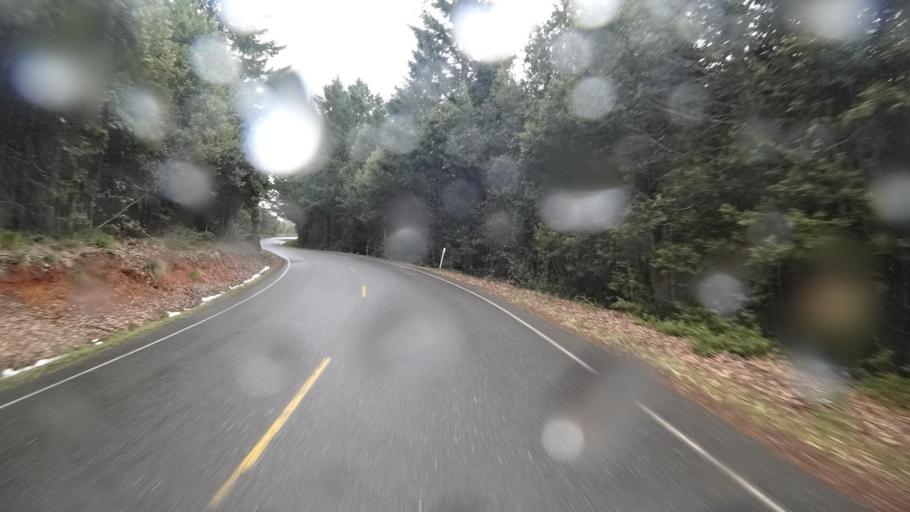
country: US
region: California
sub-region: Humboldt County
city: Willow Creek
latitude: 41.1847
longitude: -123.8151
